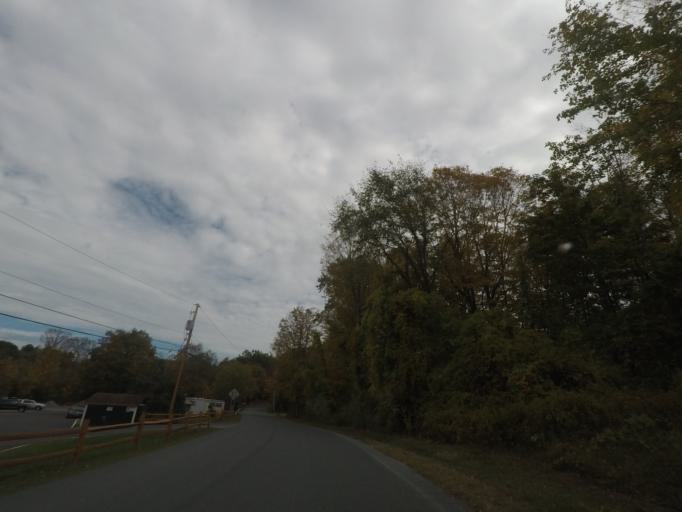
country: US
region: New York
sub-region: Rensselaer County
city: East Greenbush
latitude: 42.5556
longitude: -73.6590
